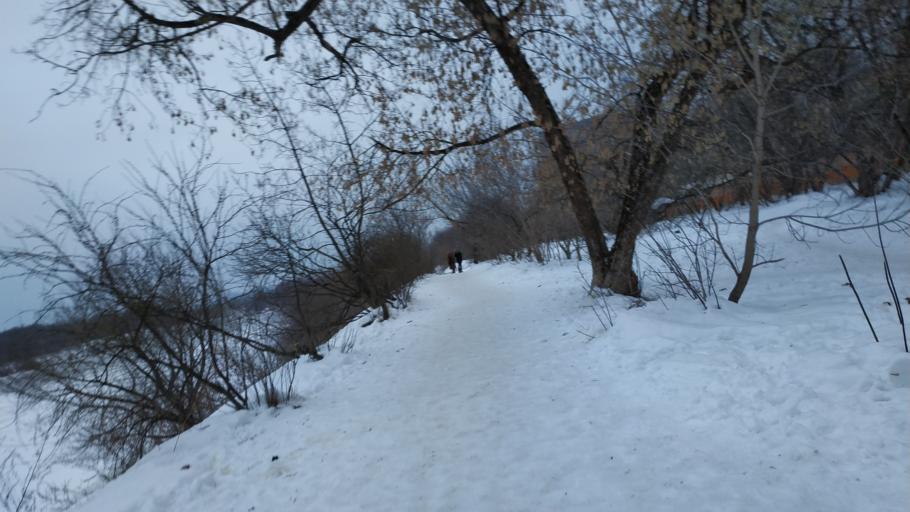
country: RU
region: Moscow
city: Shchukino
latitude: 55.7892
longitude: 37.4469
